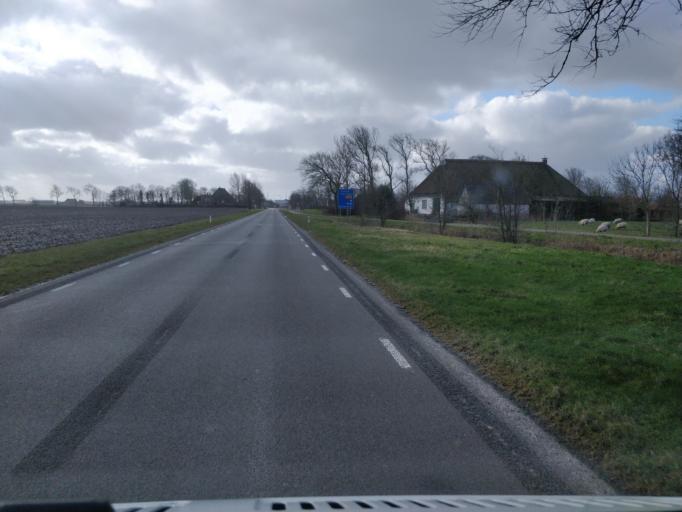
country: NL
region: Friesland
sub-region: Gemeente Franekeradeel
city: Sexbierum
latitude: 53.2037
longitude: 5.4534
